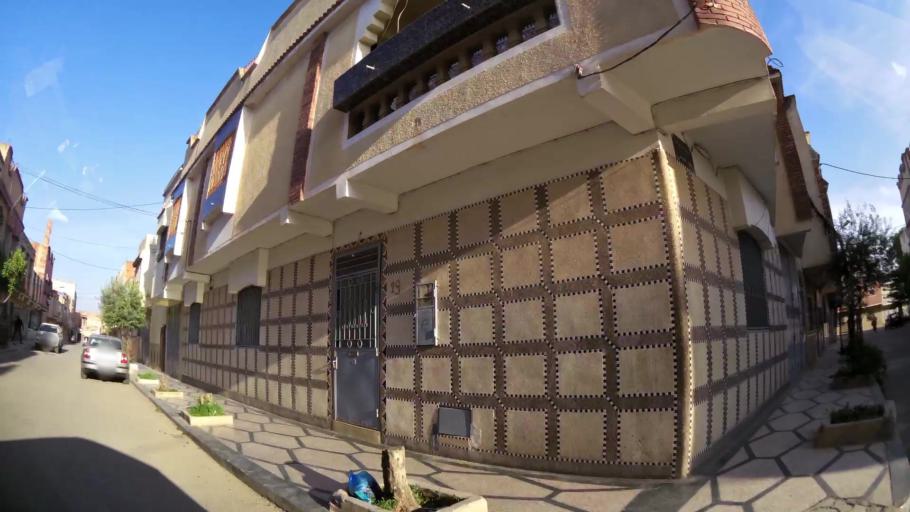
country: MA
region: Oriental
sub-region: Oujda-Angad
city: Oujda
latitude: 34.7059
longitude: -1.8990
